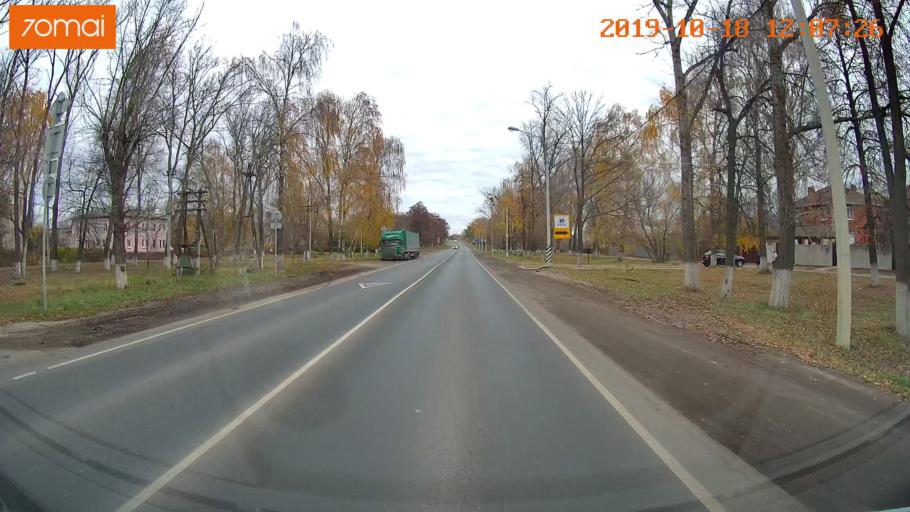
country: RU
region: Rjazan
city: Zakharovo
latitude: 54.3692
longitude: 39.2795
